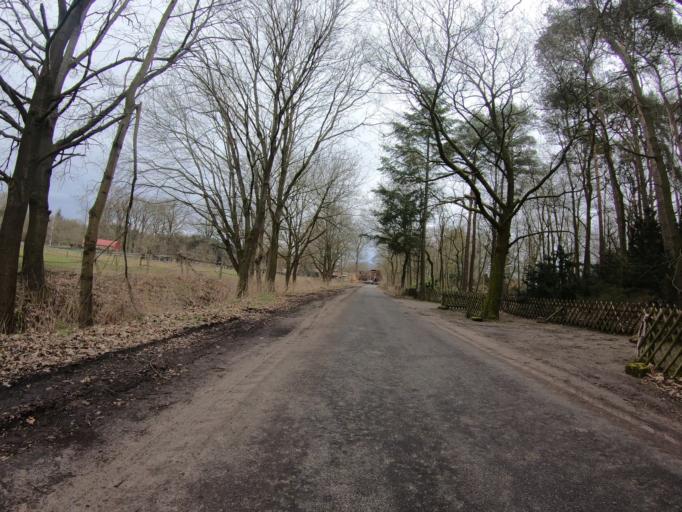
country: DE
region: Lower Saxony
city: Leiferde
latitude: 52.4806
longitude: 10.4581
